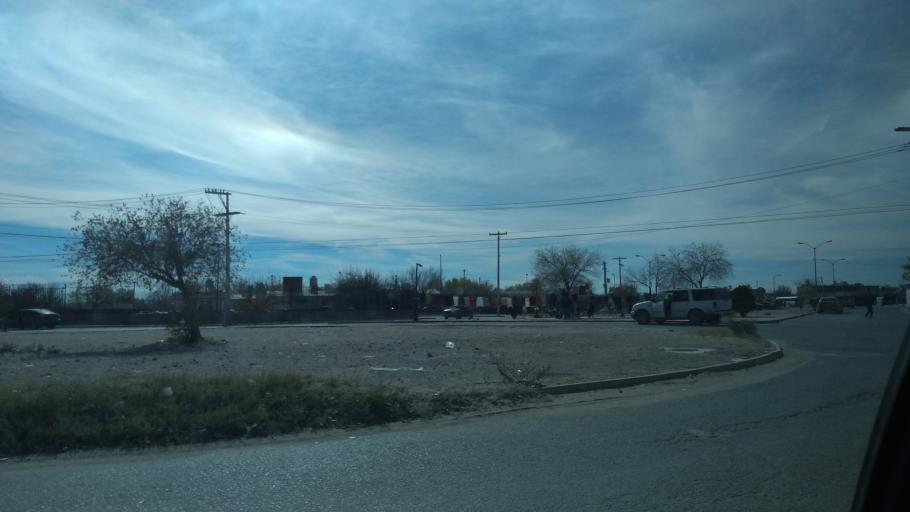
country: US
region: Texas
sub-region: El Paso County
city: Socorro Mission Number 1 Colonia
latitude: 31.5847
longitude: -106.3728
